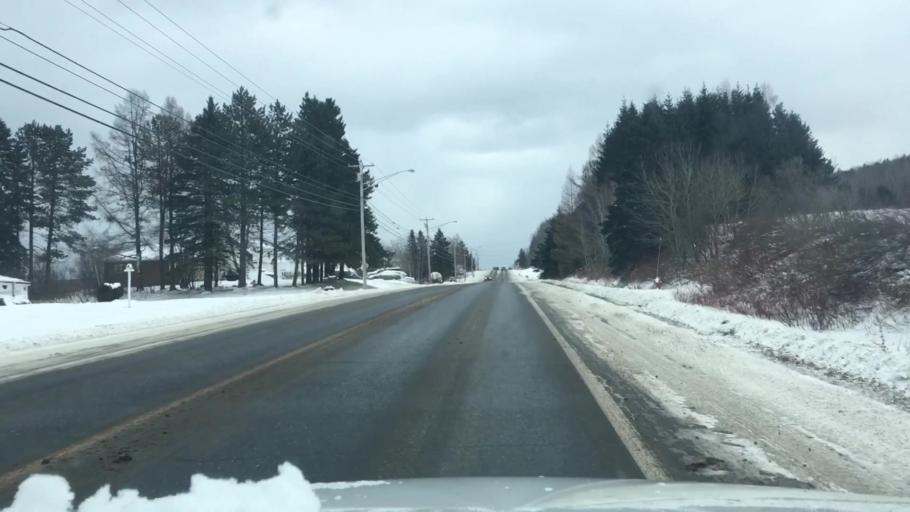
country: US
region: Maine
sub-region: Aroostook County
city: Madawaska
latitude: 47.3518
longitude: -68.2931
